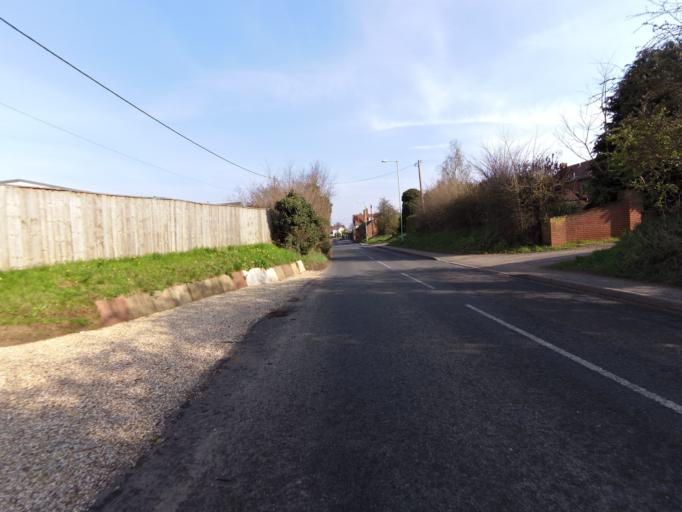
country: GB
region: England
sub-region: Suffolk
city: Bramford
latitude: 52.0749
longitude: 1.1072
